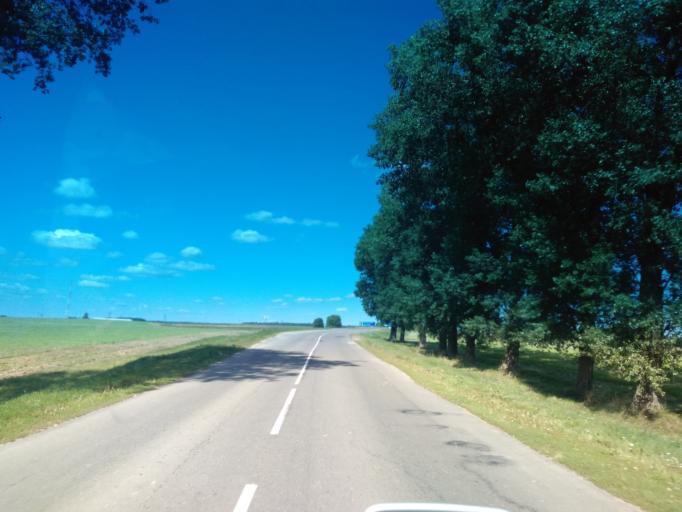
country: BY
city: Fanipol
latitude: 53.6875
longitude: 27.3627
